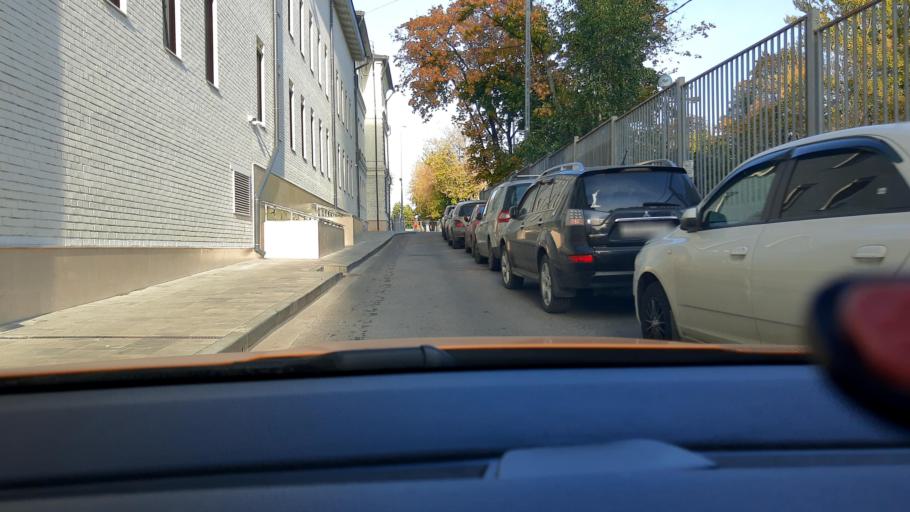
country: RU
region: Moscow
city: Sokol'niki
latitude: 55.7828
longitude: 37.6617
